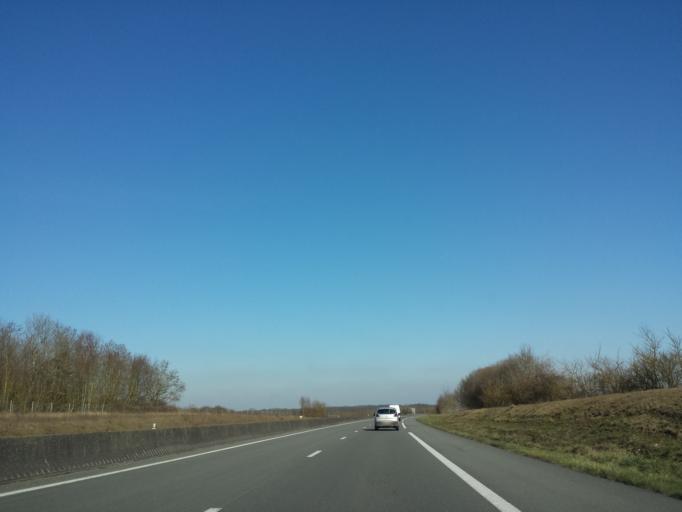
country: FR
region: Picardie
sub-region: Departement de l'Oise
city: Breteuil
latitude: 49.6291
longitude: 2.2086
